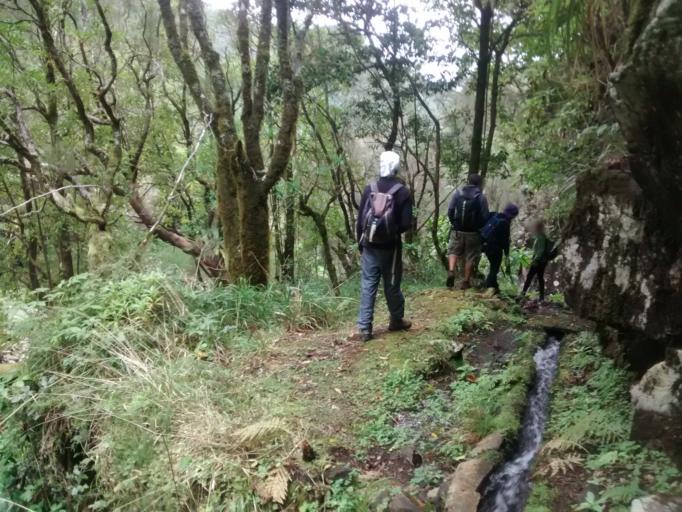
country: PT
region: Madeira
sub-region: Sao Vicente
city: Sao Vicente
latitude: 32.7576
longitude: -17.0476
